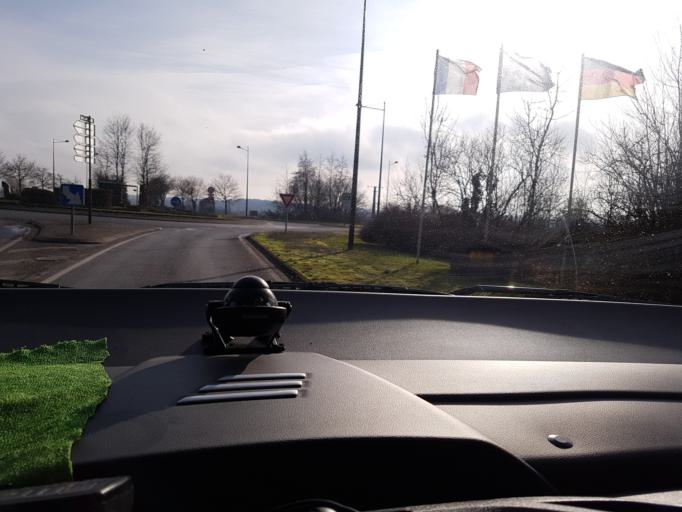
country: FR
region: Picardie
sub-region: Departement de l'Aisne
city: Hirson
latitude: 49.9386
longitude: 4.0709
